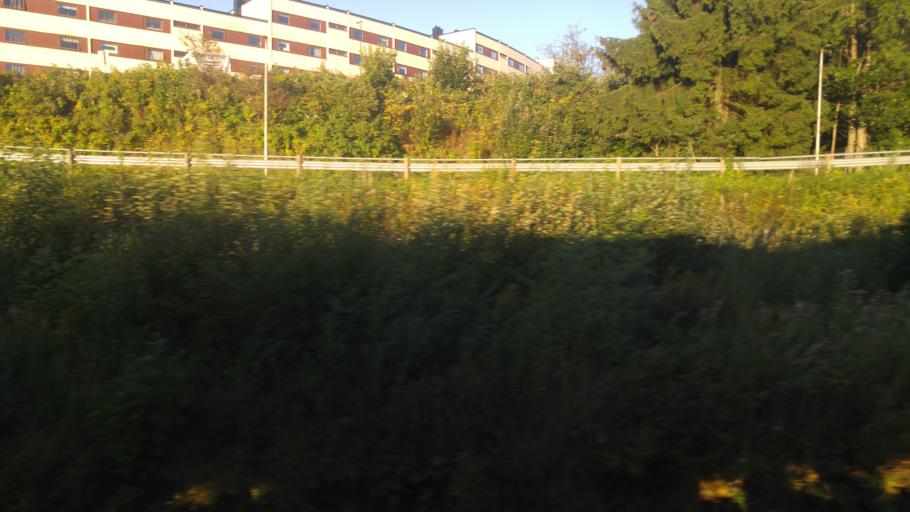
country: NO
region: Akershus
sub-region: Skedsmo
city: Lillestrom
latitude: 59.9548
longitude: 11.0201
